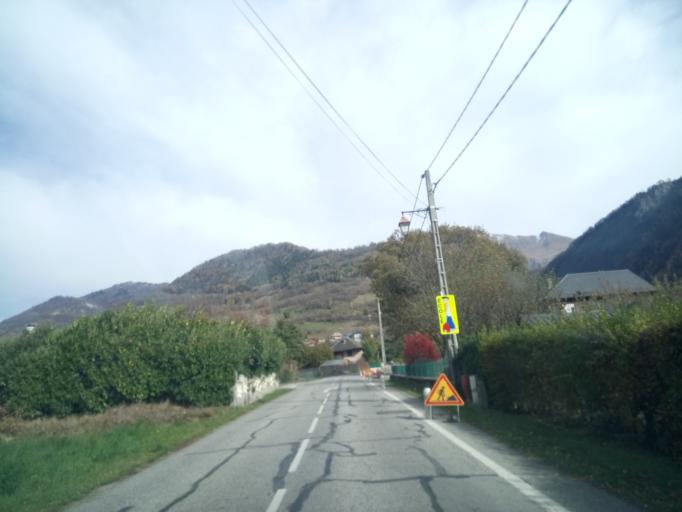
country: FR
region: Rhone-Alpes
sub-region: Departement de la Savoie
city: La Chambre
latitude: 45.3638
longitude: 6.3080
